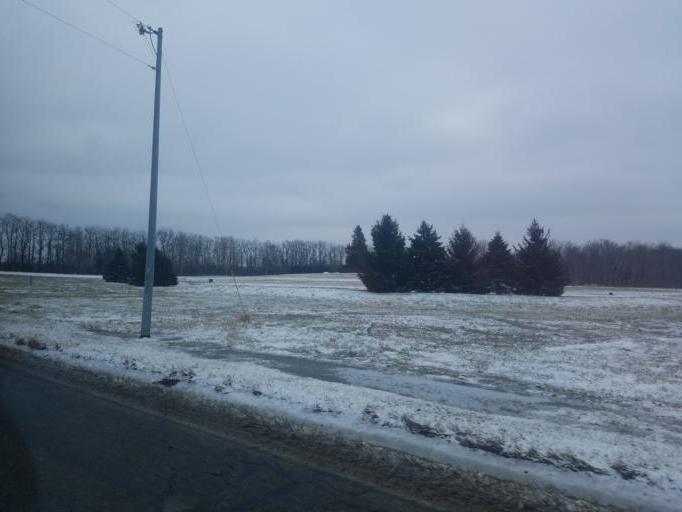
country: US
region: Ohio
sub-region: Franklin County
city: New Albany
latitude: 40.0481
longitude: -82.7624
